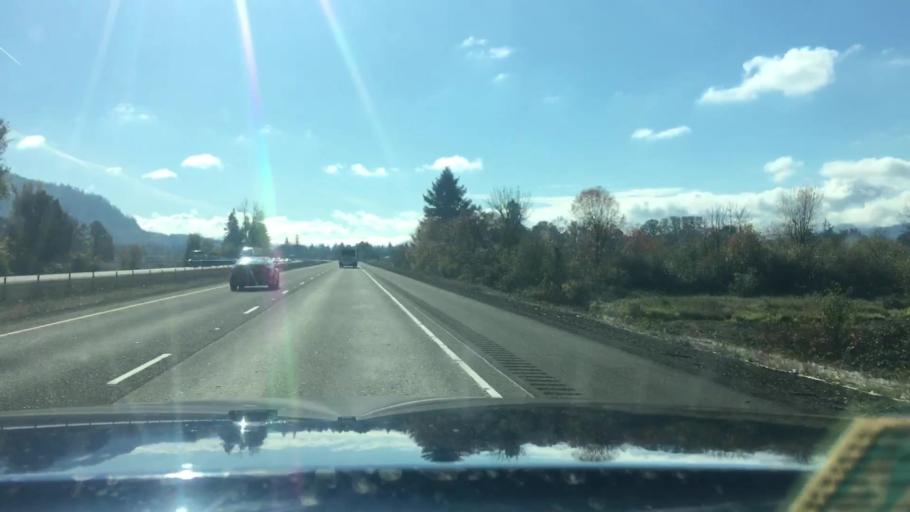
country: US
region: Oregon
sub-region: Lane County
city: Creswell
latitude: 43.9045
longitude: -123.0143
